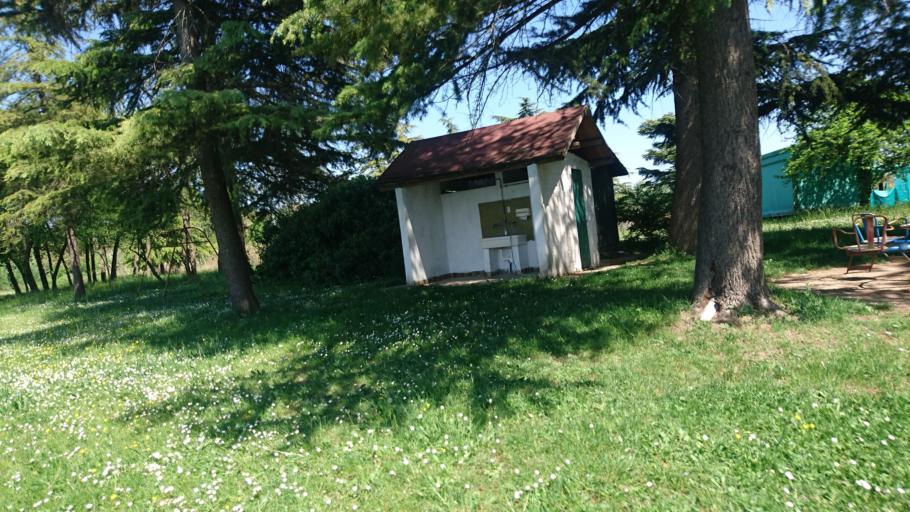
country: IT
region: Veneto
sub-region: Provincia di Treviso
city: Casier
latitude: 45.6461
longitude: 12.2858
